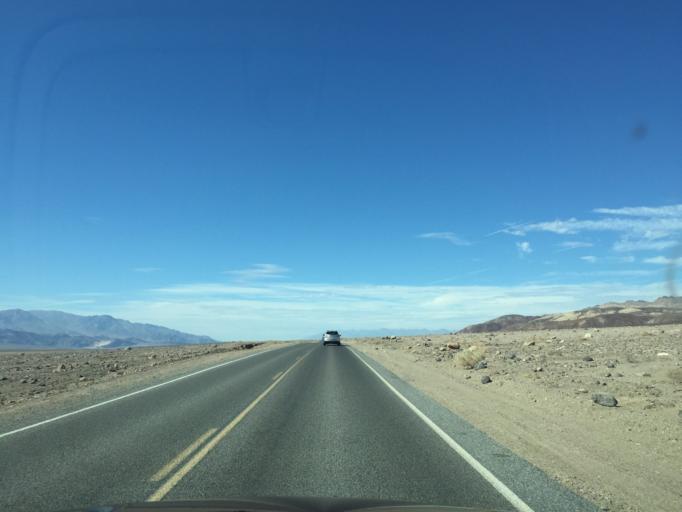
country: US
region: Nevada
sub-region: Nye County
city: Beatty
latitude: 36.2943
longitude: -116.8093
